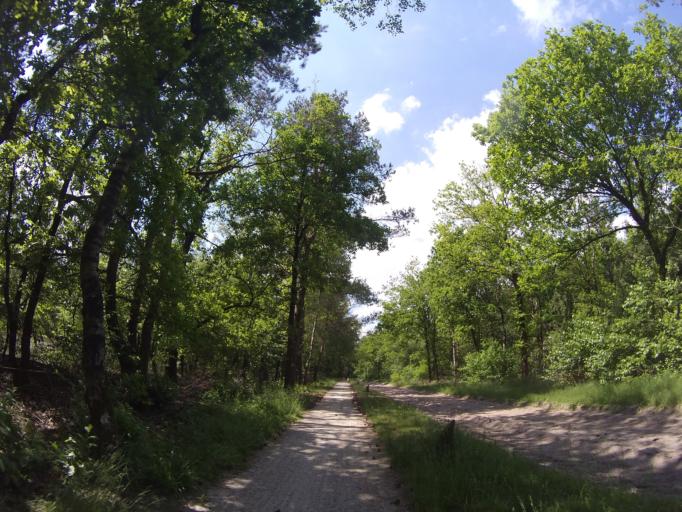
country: NL
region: Gelderland
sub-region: Gemeente Barneveld
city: Stroe
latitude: 52.1887
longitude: 5.7069
